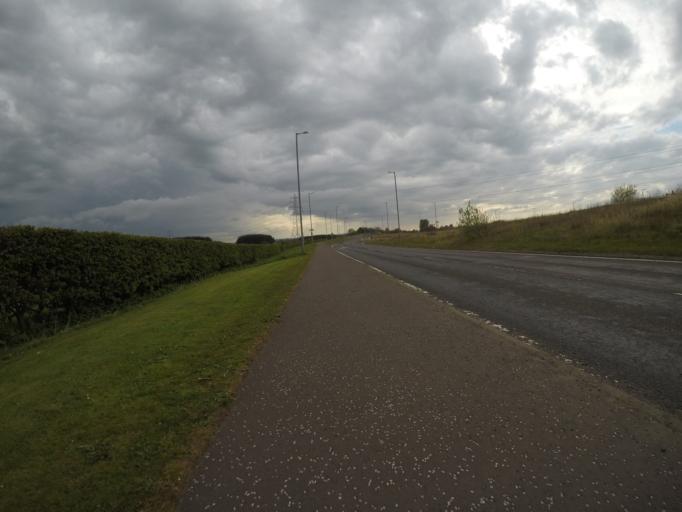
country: GB
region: Scotland
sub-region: East Ayrshire
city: Kilmarnock
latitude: 55.6443
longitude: -4.4598
